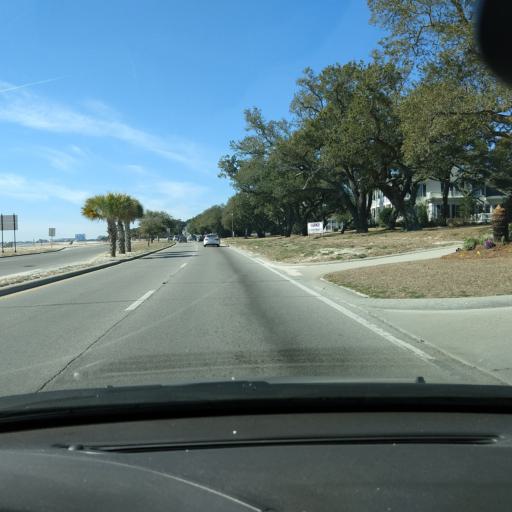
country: US
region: Mississippi
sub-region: Harrison County
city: Gulfport
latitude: 30.3750
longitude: -89.0612
